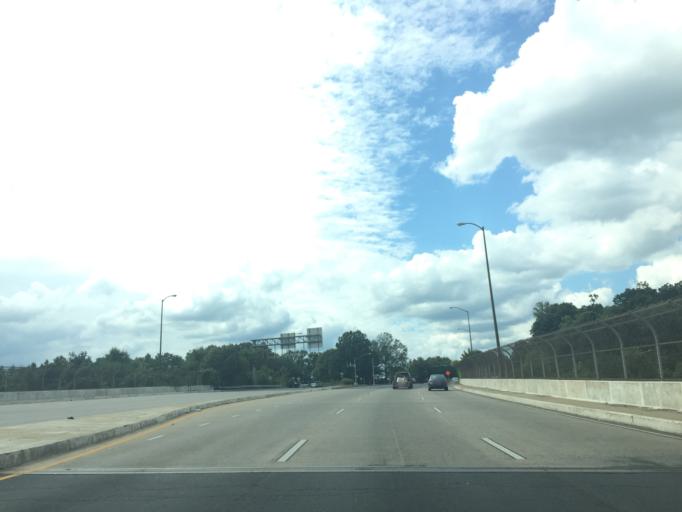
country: US
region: Maryland
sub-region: Montgomery County
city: Derwood
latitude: 39.1307
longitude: -77.1619
